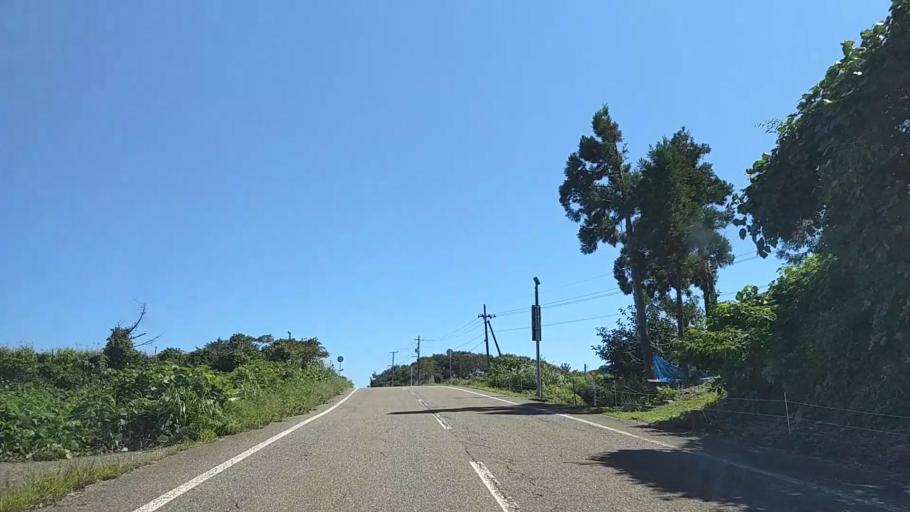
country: JP
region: Niigata
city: Joetsu
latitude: 37.1711
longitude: 138.1044
